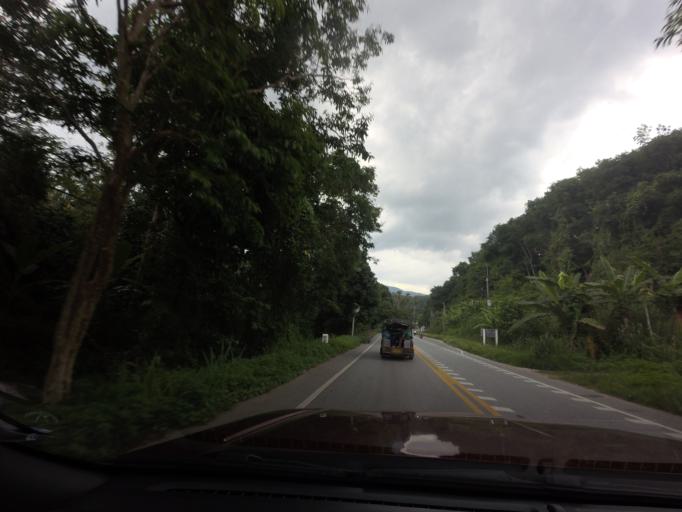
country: TH
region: Yala
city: Than To
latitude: 6.2317
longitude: 101.1667
